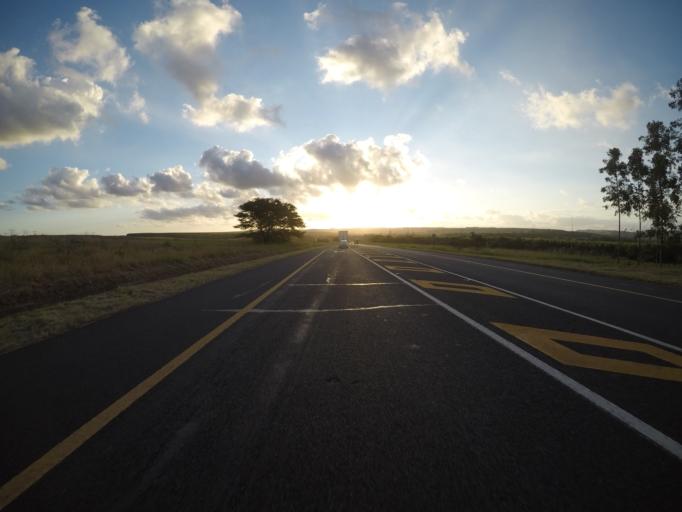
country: ZA
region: KwaZulu-Natal
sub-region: uThungulu District Municipality
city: Richards Bay
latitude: -28.6957
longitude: 32.0203
